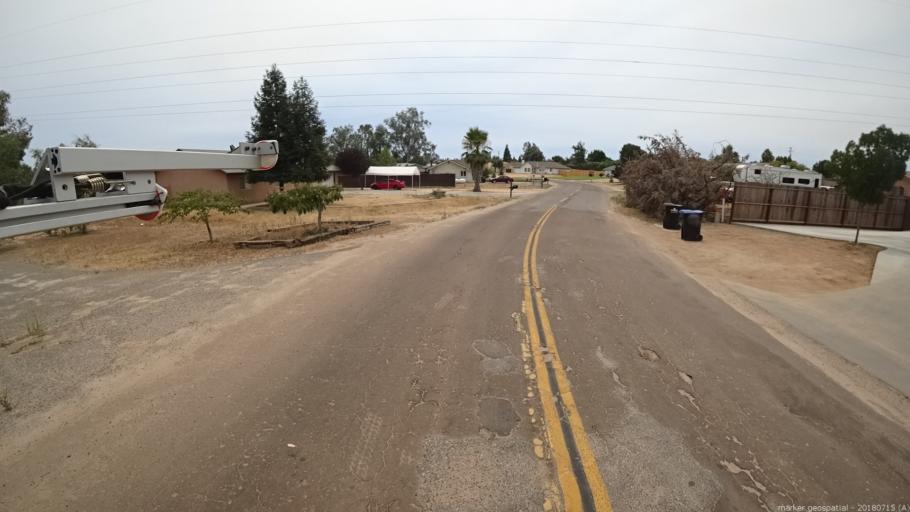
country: US
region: California
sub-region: Madera County
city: Madera Acres
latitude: 37.0149
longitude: -120.0790
